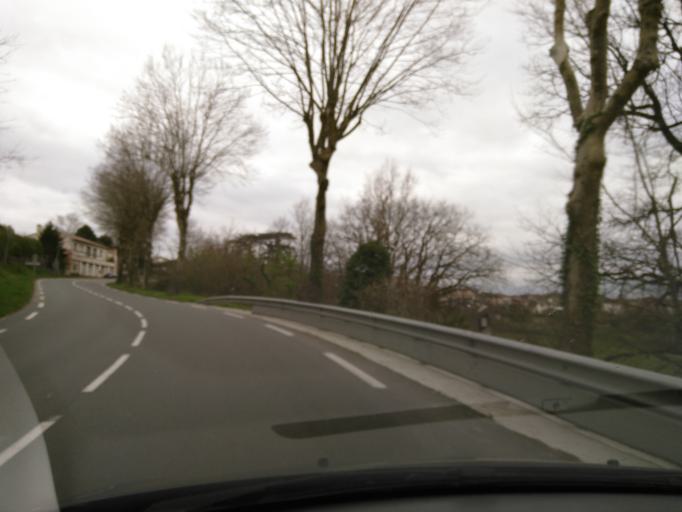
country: FR
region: Aquitaine
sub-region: Departement du Lot-et-Garonne
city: Cancon
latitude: 44.4950
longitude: 0.6690
